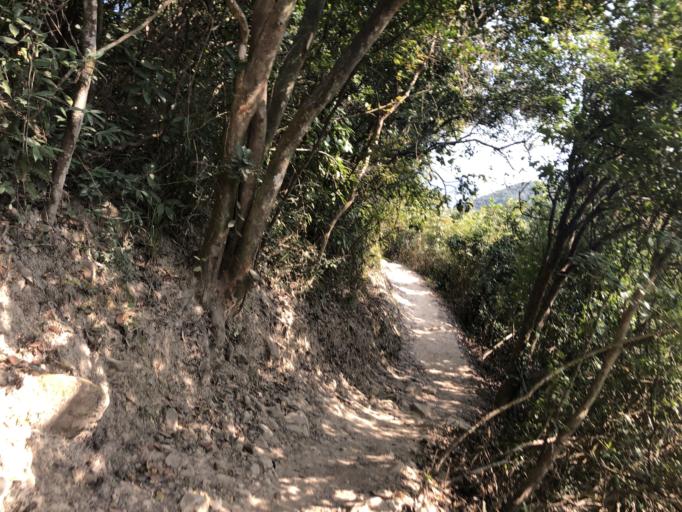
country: HK
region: Sai Kung
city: Sai Kung
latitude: 22.3653
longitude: 114.2911
